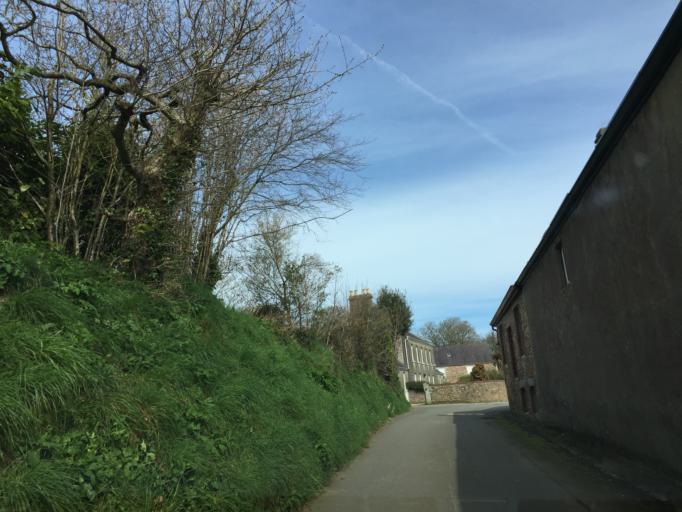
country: JE
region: St Helier
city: Saint Helier
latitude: 49.2404
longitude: -2.1785
